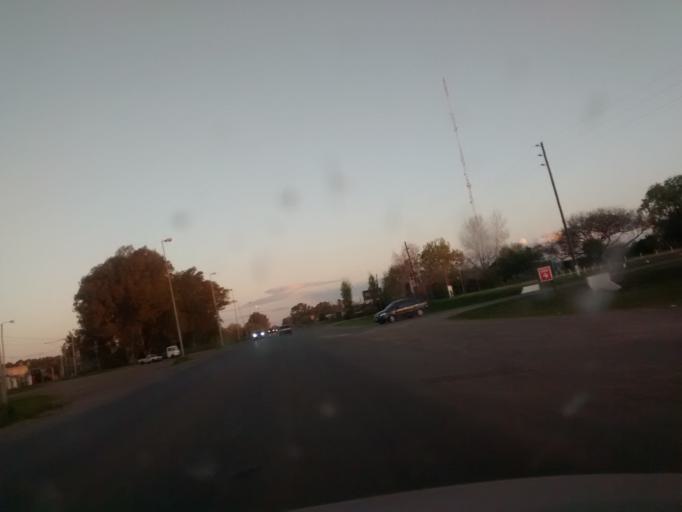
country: AR
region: Buenos Aires
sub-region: Partido de La Plata
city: La Plata
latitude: -34.9967
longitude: -58.0330
